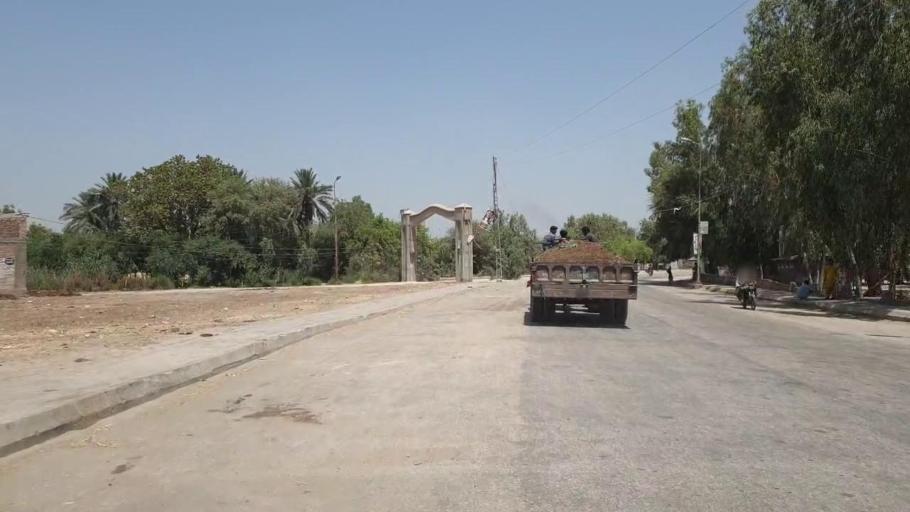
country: PK
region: Sindh
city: Adilpur
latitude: 27.9396
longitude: 69.3186
